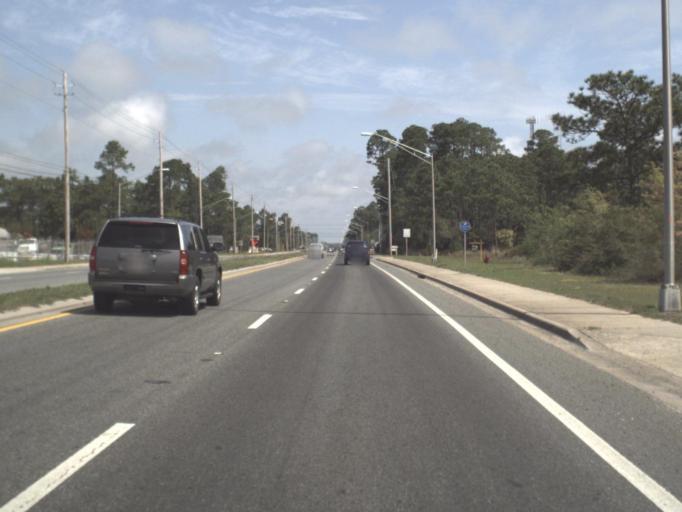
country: US
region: Florida
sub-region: Santa Rosa County
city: Navarre
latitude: 30.4106
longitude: -86.8700
